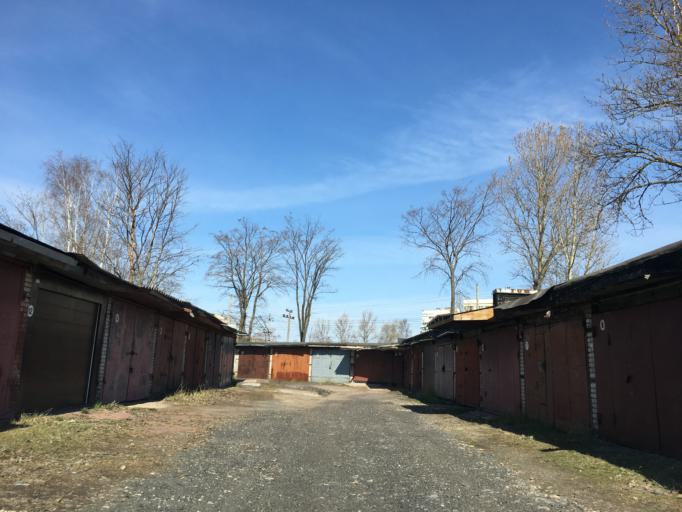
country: RU
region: St.-Petersburg
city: Uritsk
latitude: 59.8231
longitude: 30.1695
